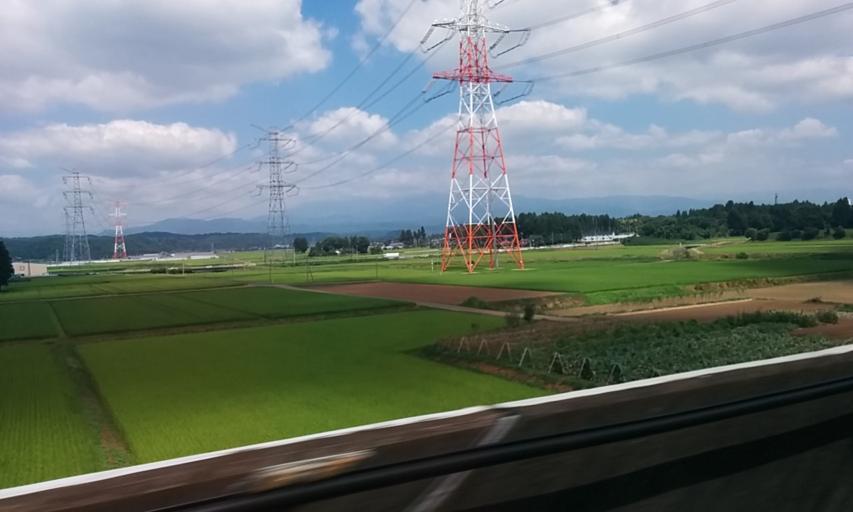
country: JP
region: Tochigi
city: Yaita
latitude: 36.7751
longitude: 139.9499
